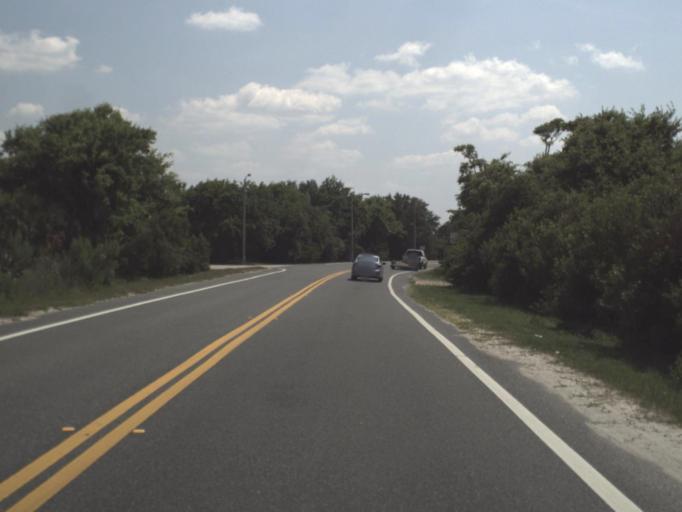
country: US
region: Florida
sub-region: Duval County
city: Atlantic Beach
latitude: 30.3855
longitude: -81.4351
